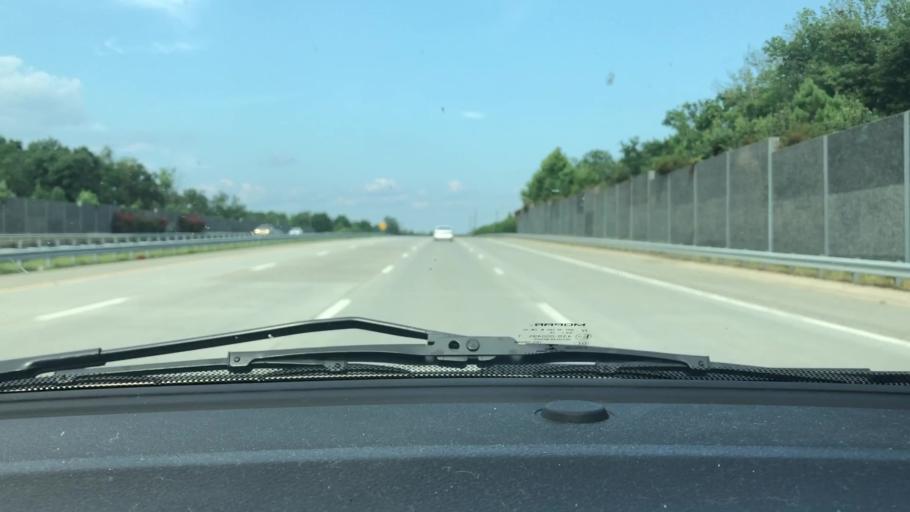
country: US
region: North Carolina
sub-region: Guilford County
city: Jamestown
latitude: 36.0201
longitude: -79.8691
